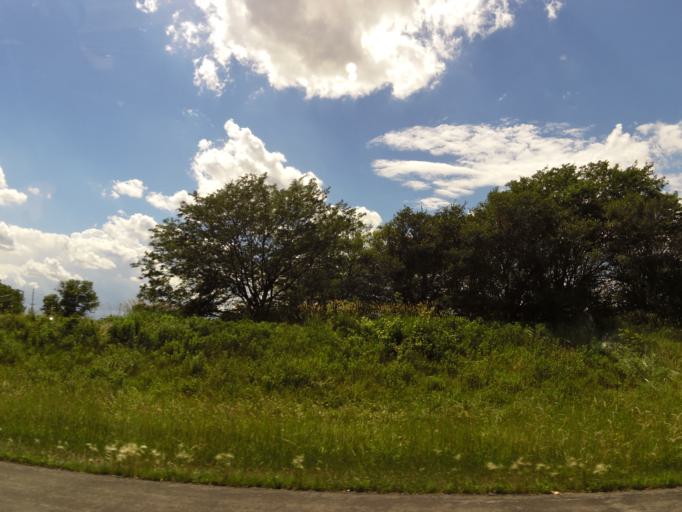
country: US
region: Iowa
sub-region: Linn County
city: Ely
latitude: 41.8923
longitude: -91.6712
